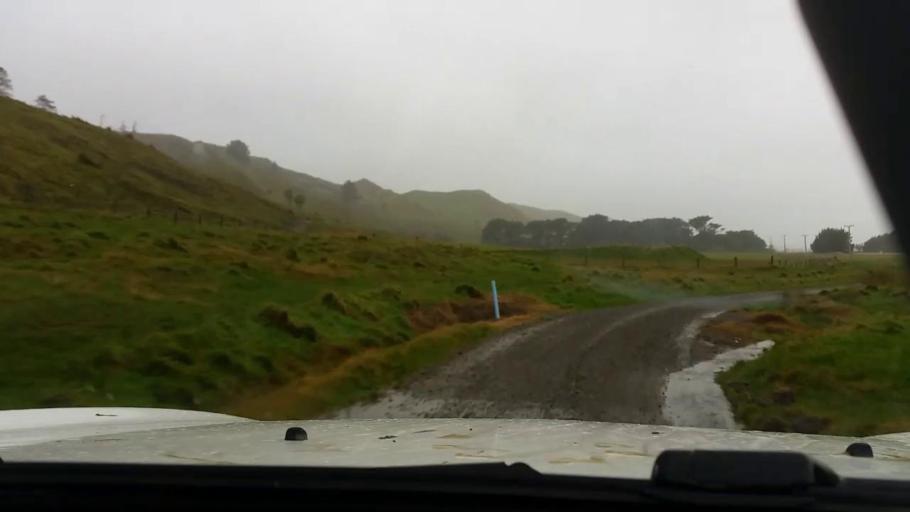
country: NZ
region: Wellington
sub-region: Masterton District
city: Masterton
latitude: -41.2597
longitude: 175.8979
